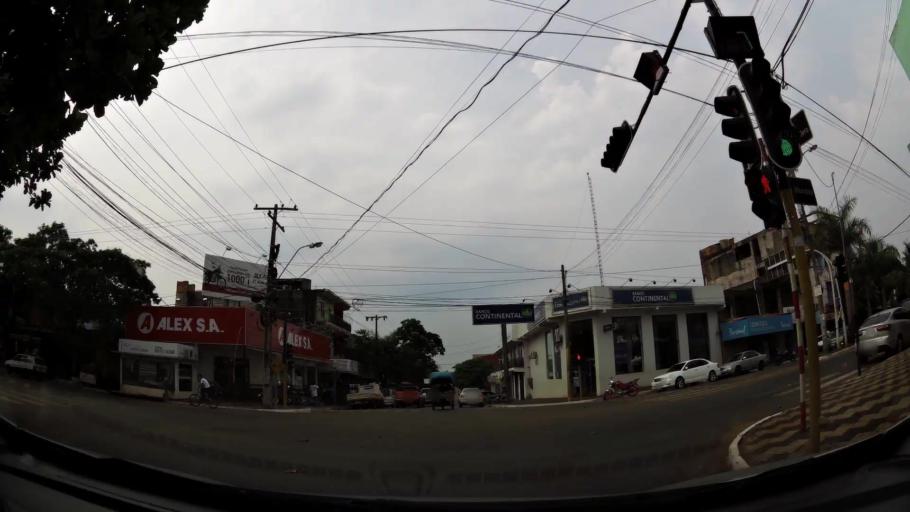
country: BR
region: Parana
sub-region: Foz Do Iguacu
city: Foz do Iguacu
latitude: -25.5586
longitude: -54.6060
